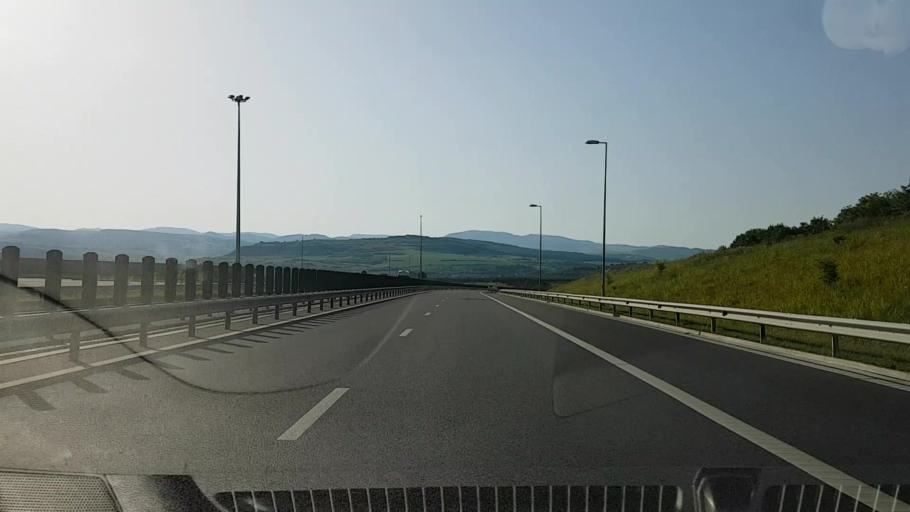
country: RO
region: Alba
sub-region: Comuna Miraslau
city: Miraslau
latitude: 46.3464
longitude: 23.7289
